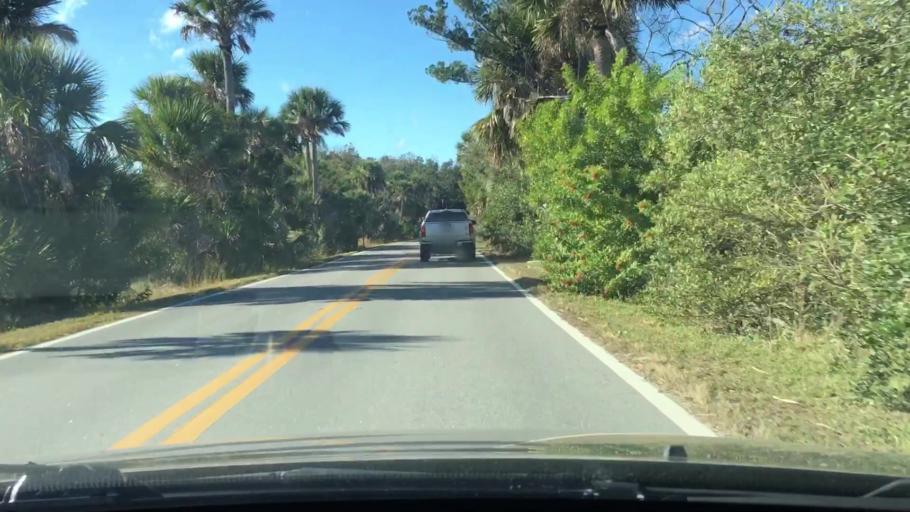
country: US
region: Florida
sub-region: Volusia County
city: Ormond-by-the-Sea
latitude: 29.3442
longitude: -81.0920
